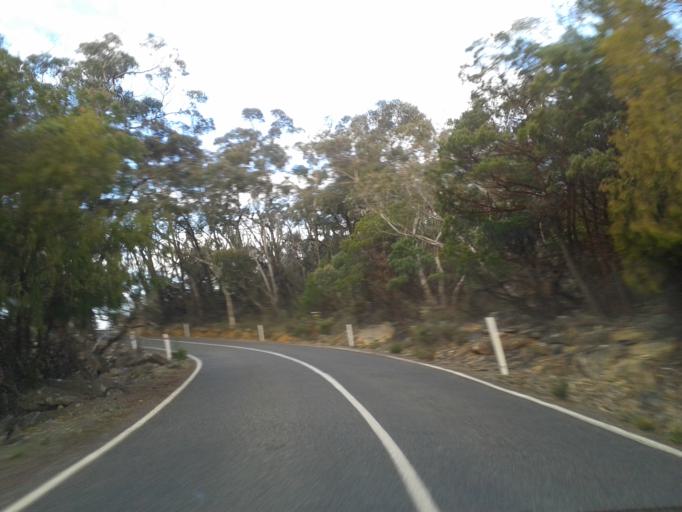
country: AU
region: Victoria
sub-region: Northern Grampians
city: Stawell
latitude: -37.1438
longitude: 142.4443
